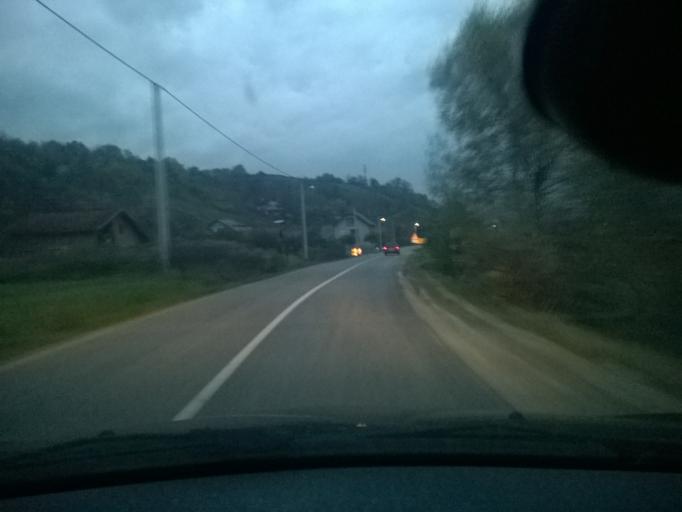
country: HR
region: Krapinsko-Zagorska
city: Zabok
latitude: 46.0632
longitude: 15.9073
